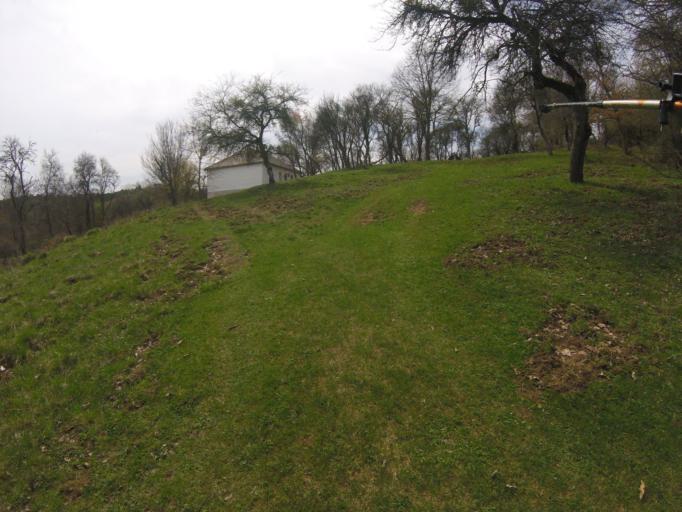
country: SK
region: Kosicky
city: Roznava
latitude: 48.5426
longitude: 20.6400
